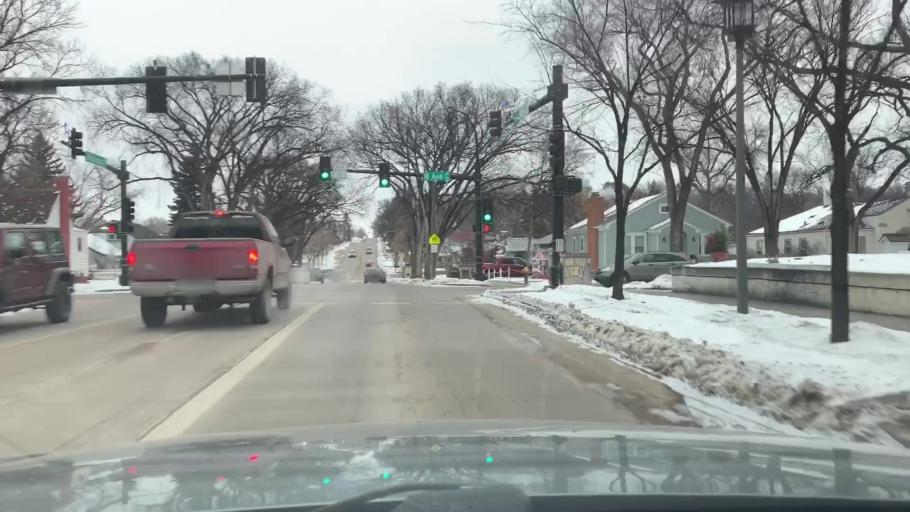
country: US
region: North Dakota
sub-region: Burleigh County
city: Bismarck
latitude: 46.8116
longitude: -100.7943
